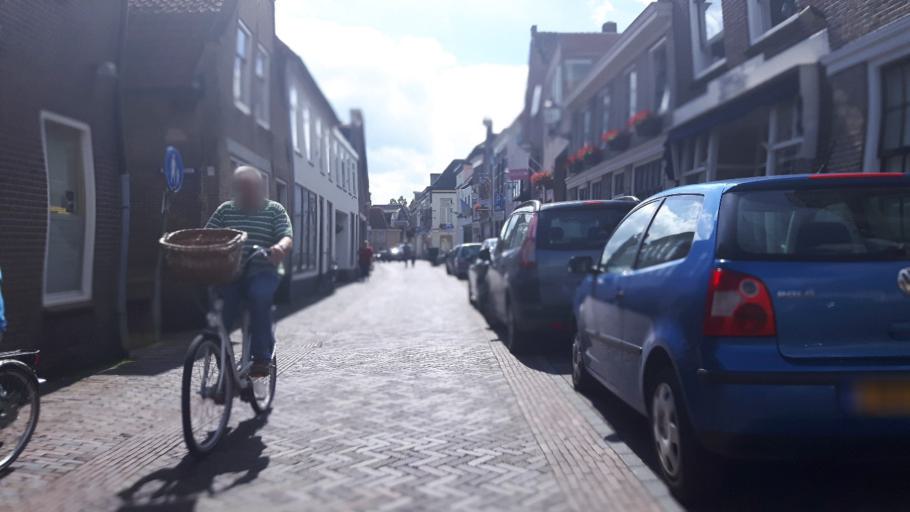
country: NL
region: South Holland
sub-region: Gemeente Vlist
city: Haastrecht
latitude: 52.0020
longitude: 4.7754
